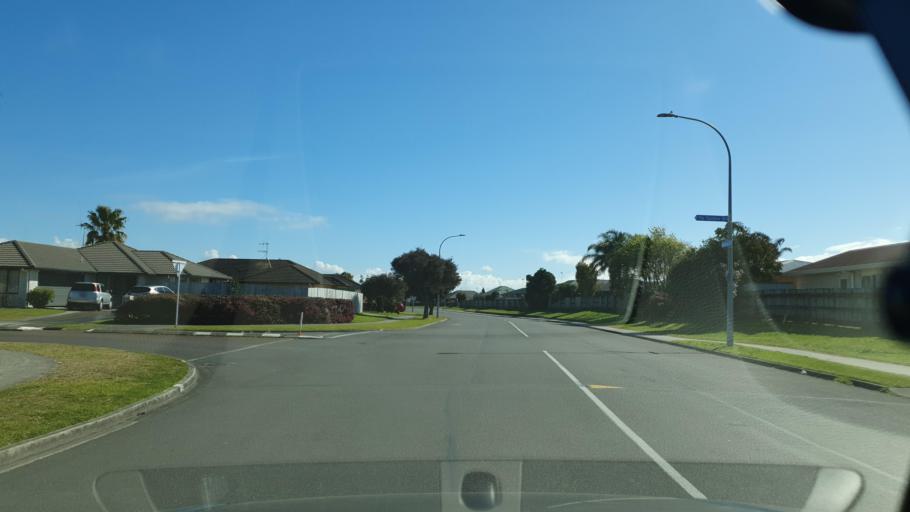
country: NZ
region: Bay of Plenty
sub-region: Tauranga City
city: Tauranga
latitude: -37.7081
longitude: 176.2935
